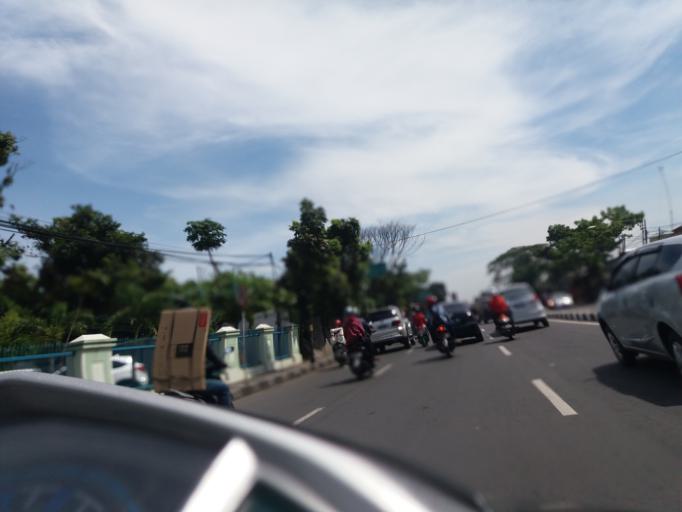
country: ID
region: West Java
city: Bandung
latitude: -6.9486
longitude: 107.6118
